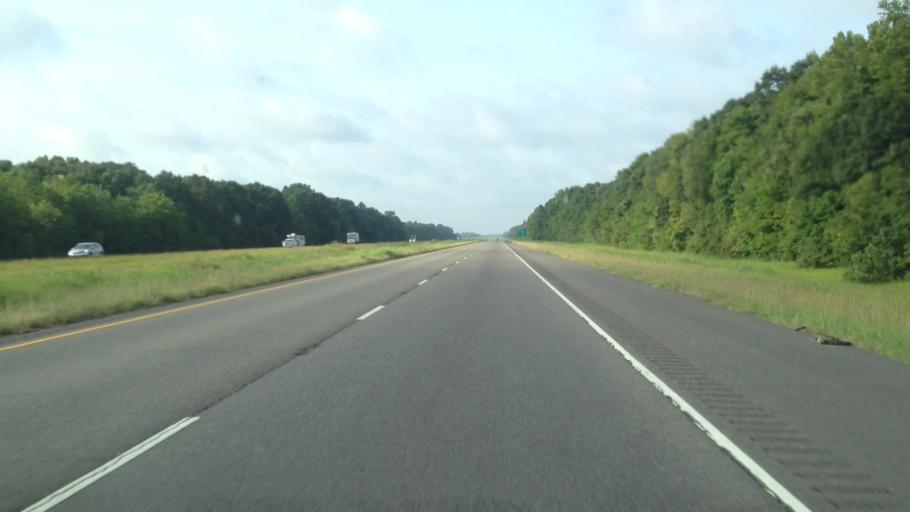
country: US
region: Louisiana
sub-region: Avoyelles Parish
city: Bunkie
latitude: 30.8907
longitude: -92.2272
